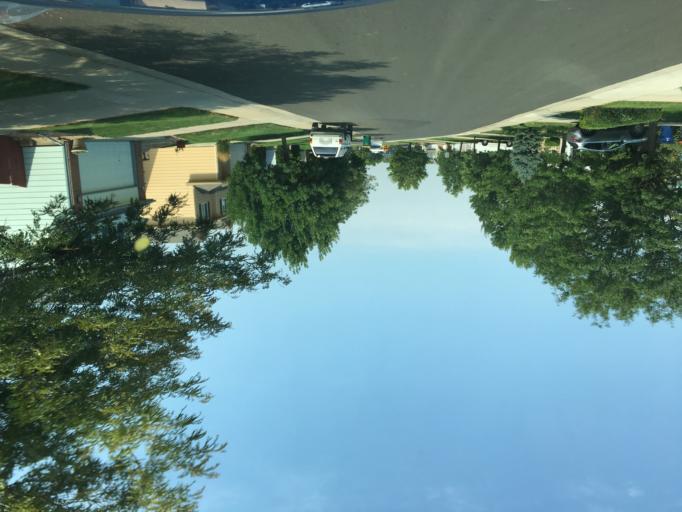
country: US
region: Colorado
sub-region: Adams County
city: Northglenn
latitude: 39.9233
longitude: -105.0179
